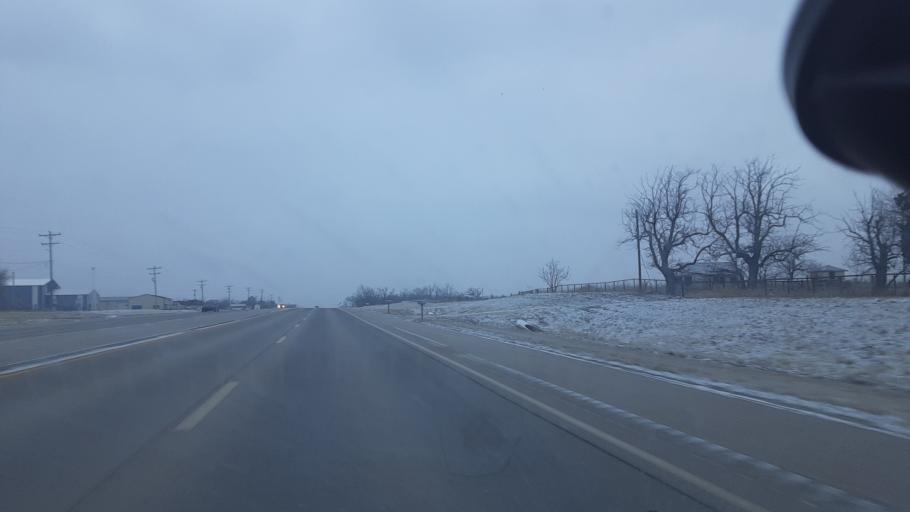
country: US
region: Oklahoma
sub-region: Payne County
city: Perkins
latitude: 35.9855
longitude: -97.0637
